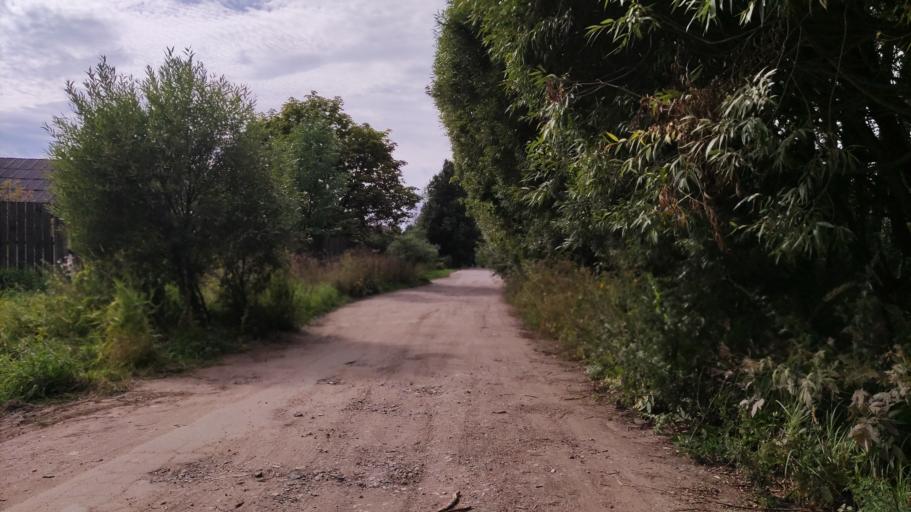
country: RU
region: Tverskaya
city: Rzhev
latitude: 56.2383
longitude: 34.3186
